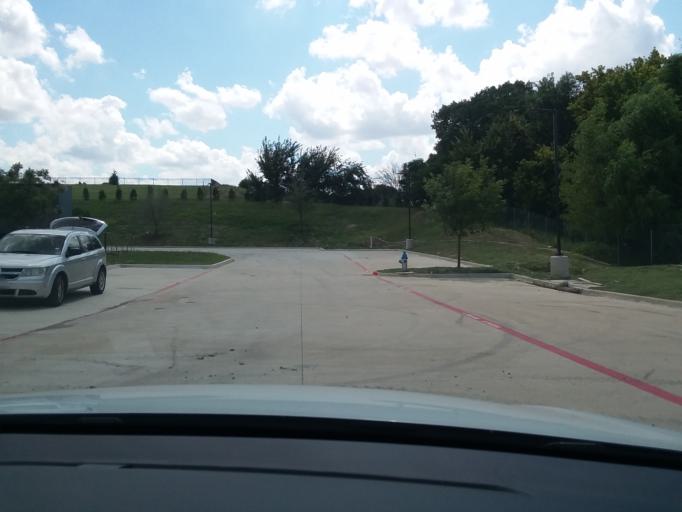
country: US
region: Texas
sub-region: Collin County
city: McKinney
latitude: 33.2178
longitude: -96.7046
